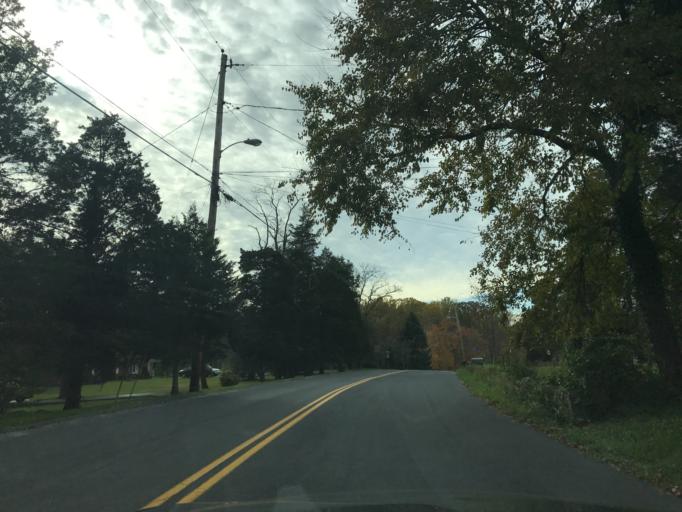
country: US
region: Maryland
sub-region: Harford County
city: Joppatowne
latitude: 39.4484
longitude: -76.3739
